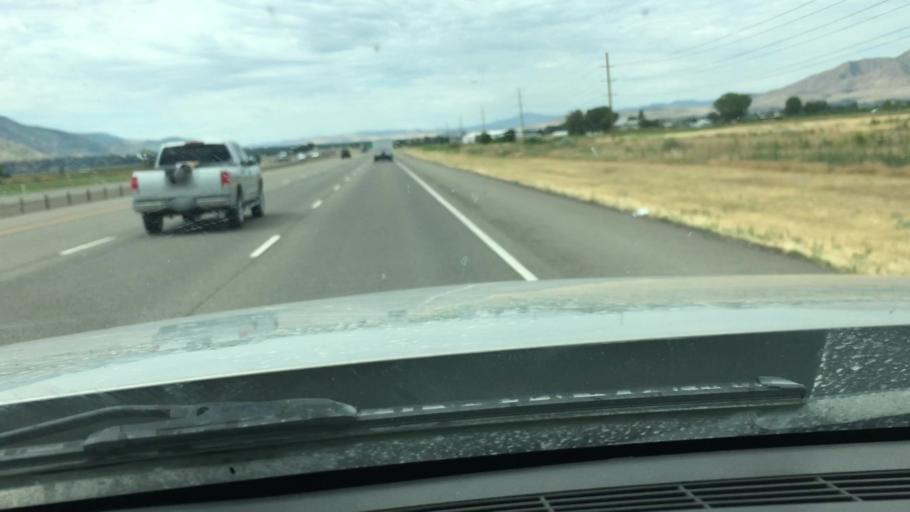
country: US
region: Utah
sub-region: Utah County
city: Benjamin
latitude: 40.0943
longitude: -111.6935
